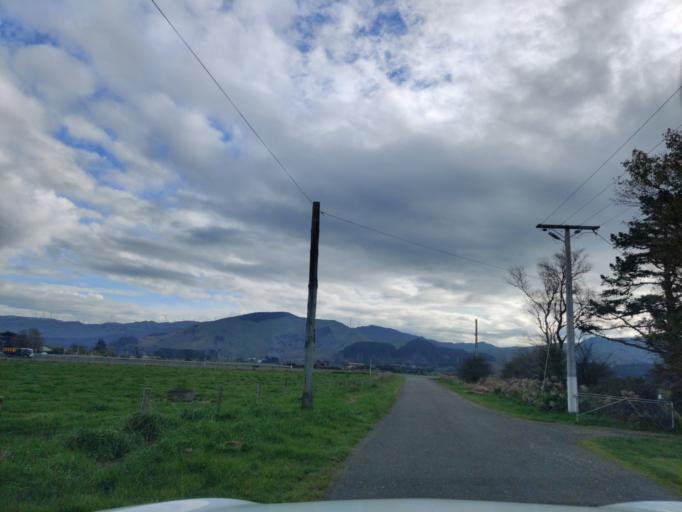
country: NZ
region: Manawatu-Wanganui
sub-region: Palmerston North City
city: Palmerston North
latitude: -40.3317
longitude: 175.8530
